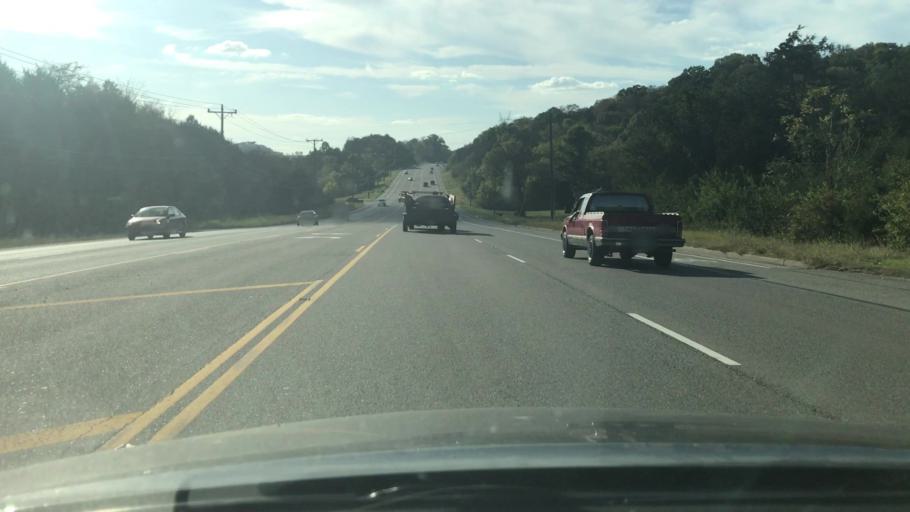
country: US
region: Tennessee
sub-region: Davidson County
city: Nashville
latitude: 36.2103
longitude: -86.8755
